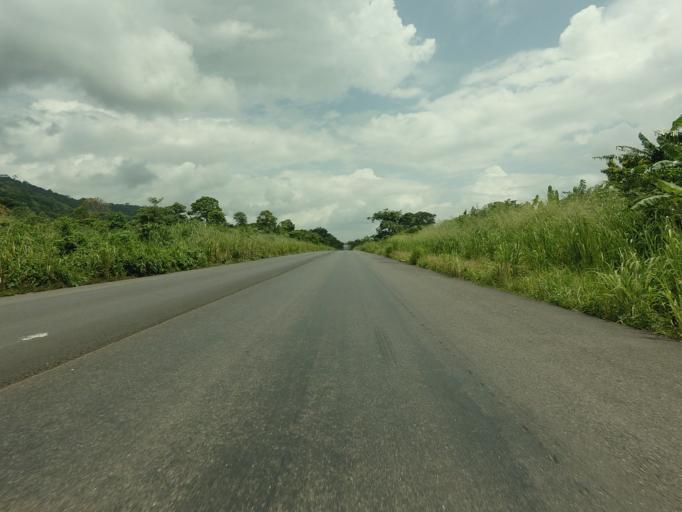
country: GH
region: Volta
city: Ho
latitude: 6.5631
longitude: 0.2661
